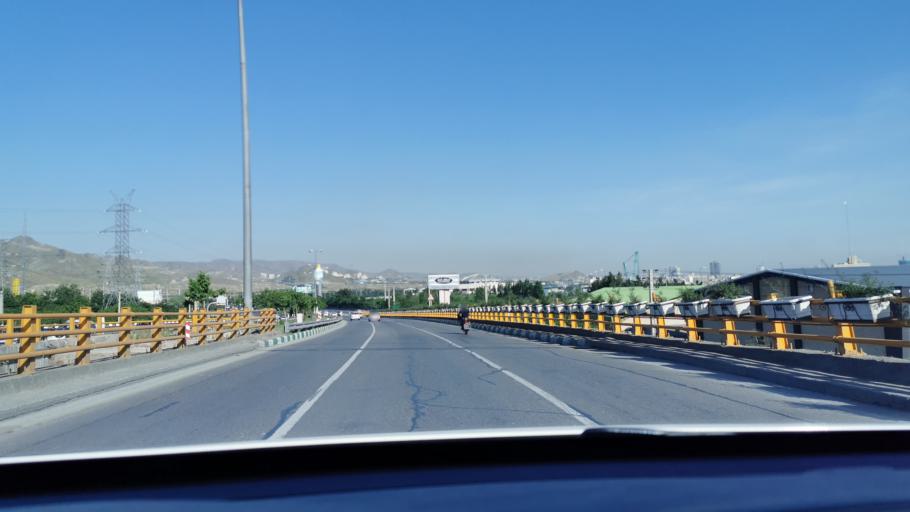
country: IR
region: Razavi Khorasan
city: Mashhad
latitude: 36.2562
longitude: 59.5982
